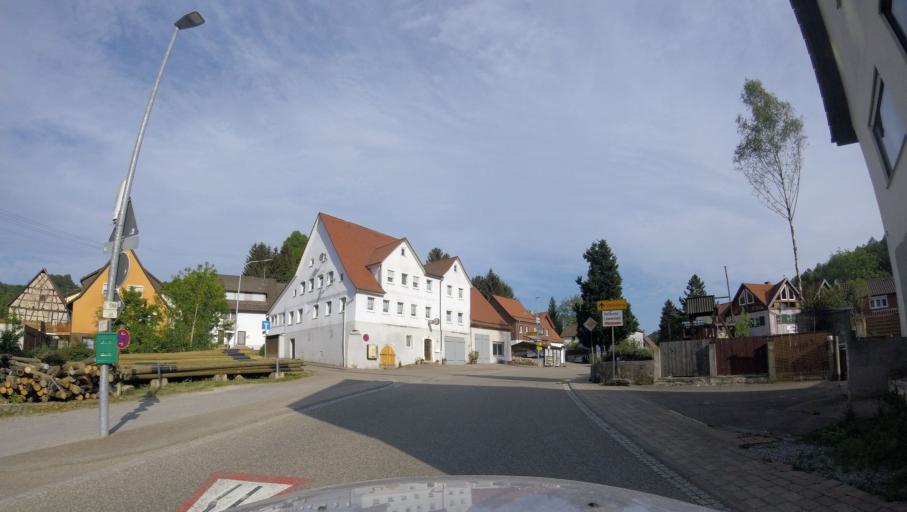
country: DE
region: Baden-Wuerttemberg
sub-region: Regierungsbezirk Stuttgart
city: Spiegelberg
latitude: 49.0599
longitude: 9.4325
